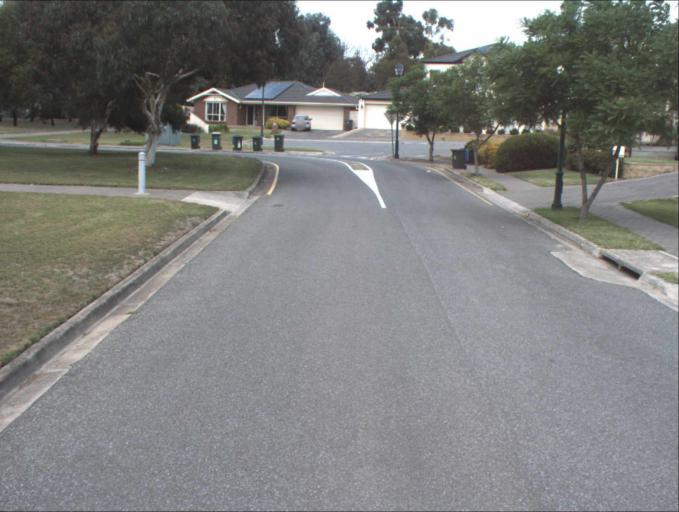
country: AU
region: South Australia
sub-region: Port Adelaide Enfield
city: Gilles Plains
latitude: -34.8452
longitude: 138.6453
